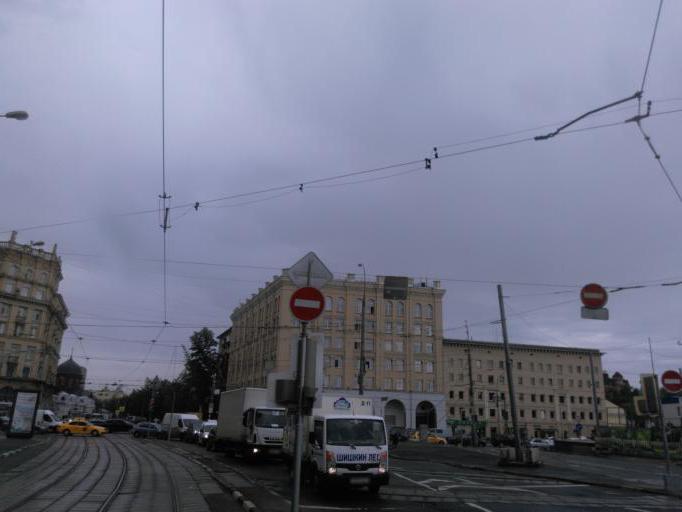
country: RU
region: Moscow
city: Zamoskvorech'ye
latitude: 55.7303
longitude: 37.6365
